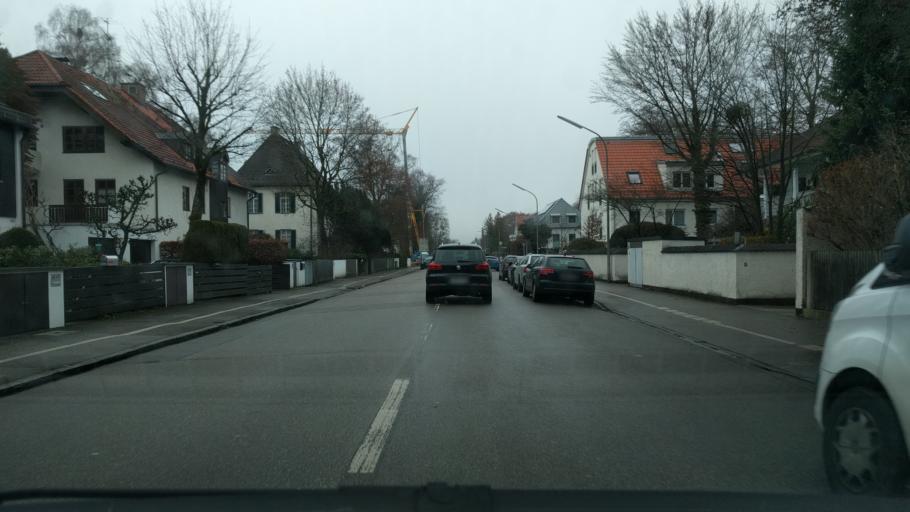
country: DE
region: Bavaria
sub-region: Upper Bavaria
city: Pullach im Isartal
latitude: 48.0843
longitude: 11.5156
